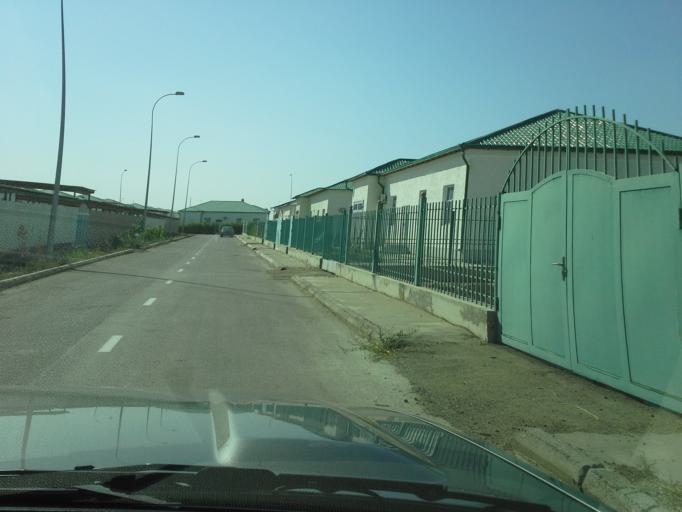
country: TM
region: Dasoguz
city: Dasoguz
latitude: 41.8161
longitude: 59.9578
